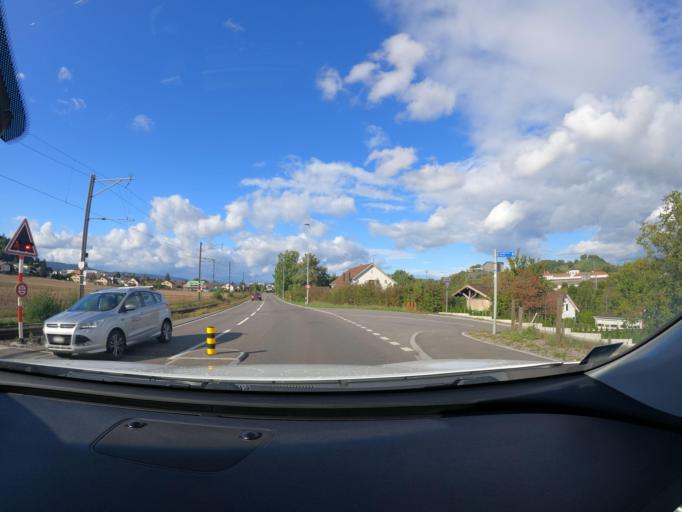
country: CH
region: Aargau
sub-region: Bezirk Lenzburg
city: Staufen
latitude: 47.3765
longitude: 8.1718
